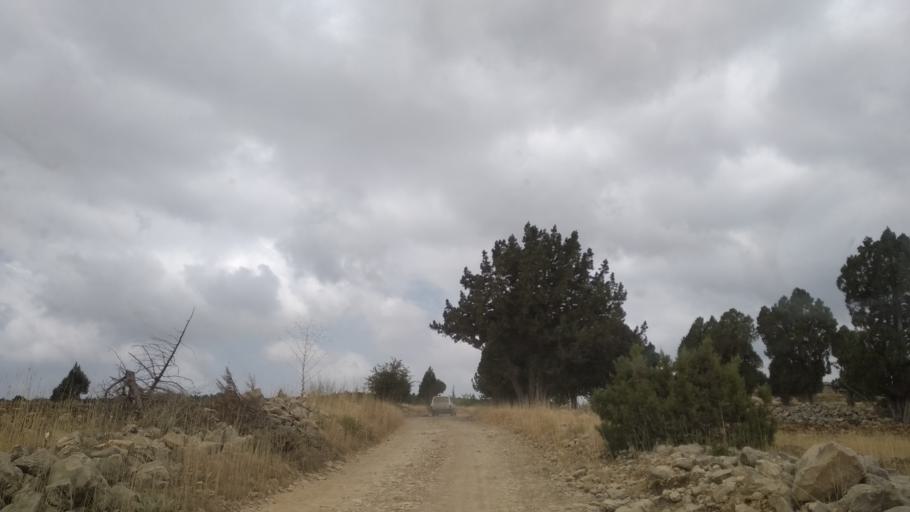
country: TR
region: Mersin
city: Sarikavak
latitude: 36.5660
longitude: 33.7661
